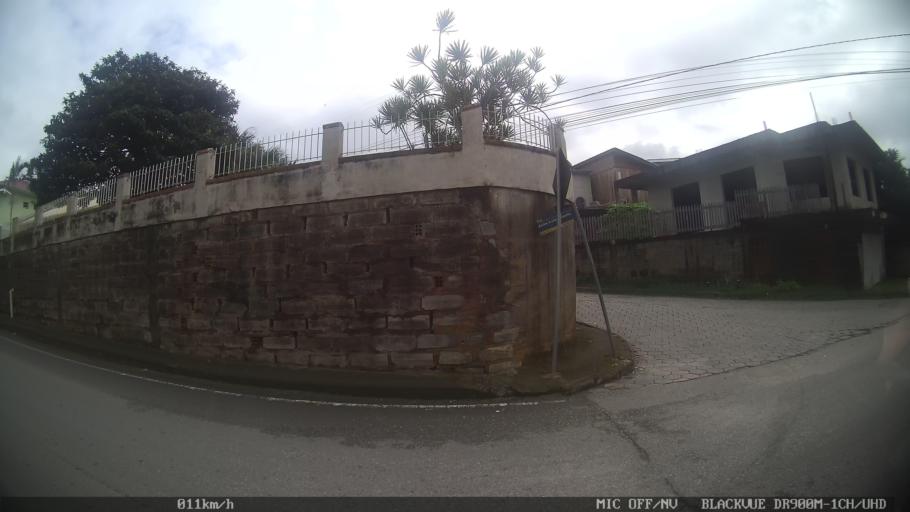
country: BR
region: Santa Catarina
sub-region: Biguacu
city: Biguacu
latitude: -27.5336
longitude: -48.6429
